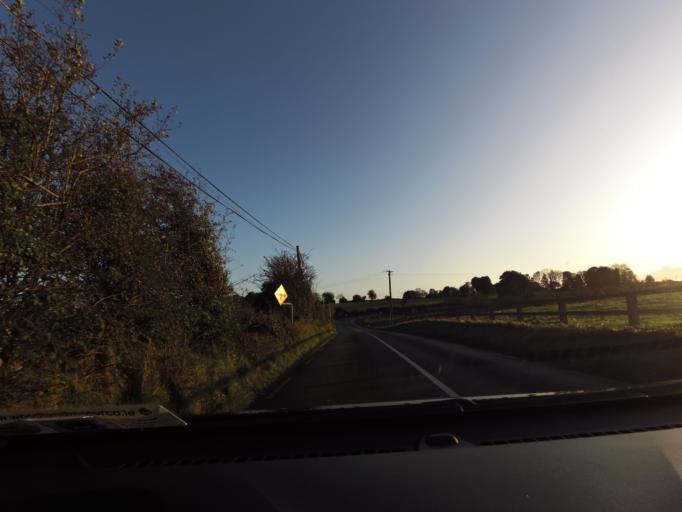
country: IE
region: Connaught
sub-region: Roscommon
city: Castlerea
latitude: 53.6848
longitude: -8.5665
